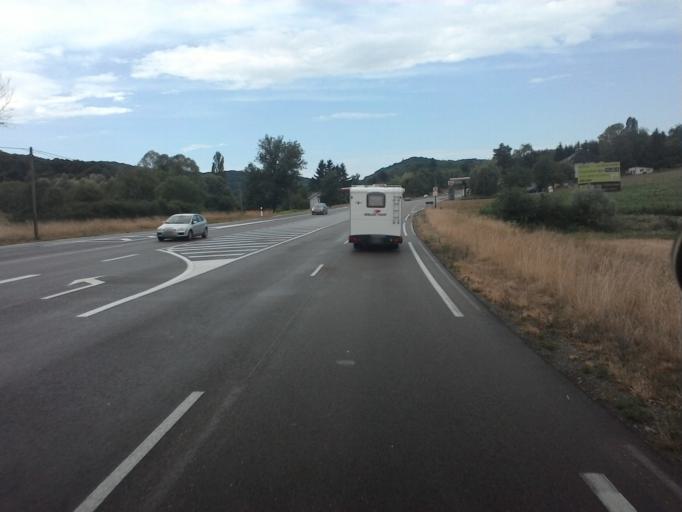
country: FR
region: Franche-Comte
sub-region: Departement du Jura
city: Poligny
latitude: 46.8086
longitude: 5.5829
